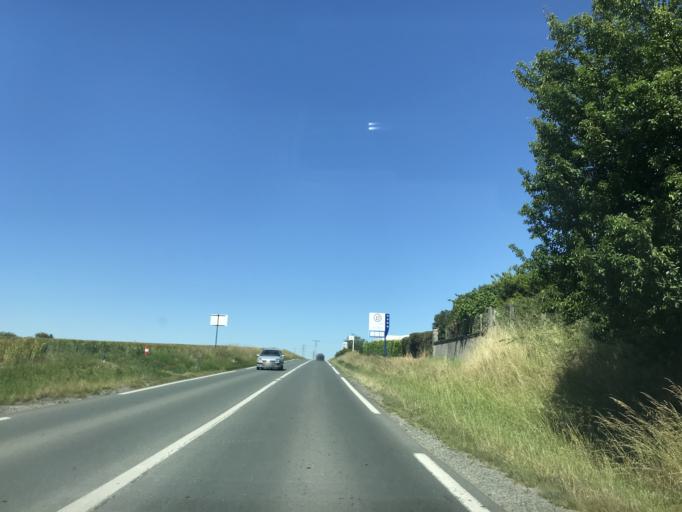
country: FR
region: Poitou-Charentes
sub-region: Departement de la Charente-Maritime
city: Pons
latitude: 45.5731
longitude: -0.5520
